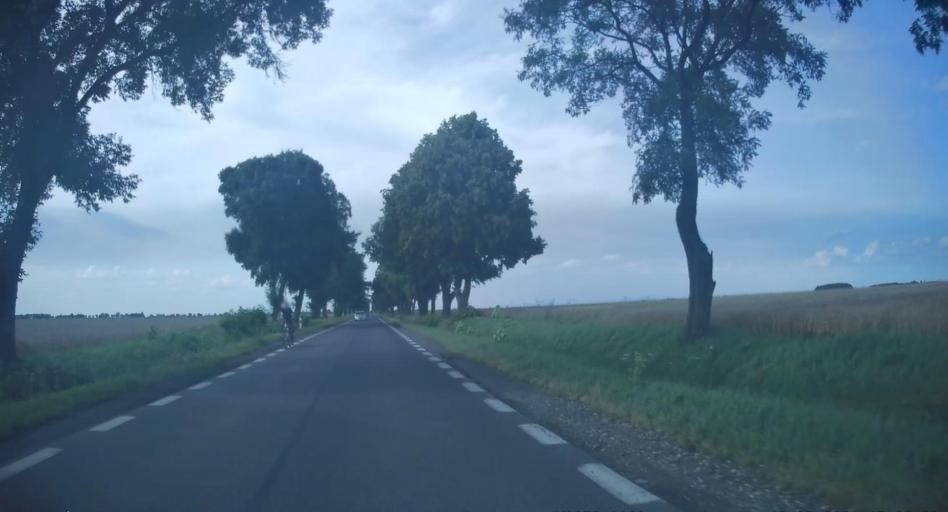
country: PL
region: Lodz Voivodeship
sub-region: Powiat tomaszowski
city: Rzeczyca
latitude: 51.6154
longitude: 20.2932
